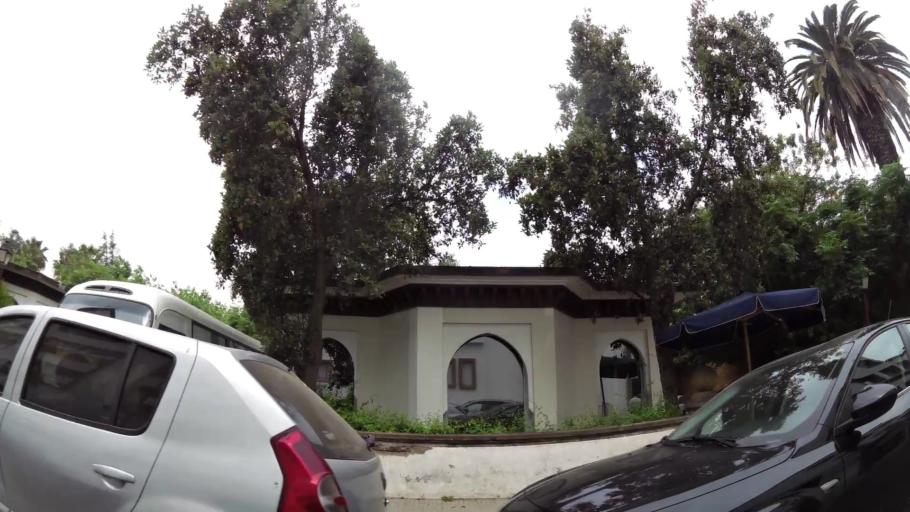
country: MA
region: Rabat-Sale-Zemmour-Zaer
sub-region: Rabat
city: Rabat
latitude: 34.0178
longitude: -6.8374
